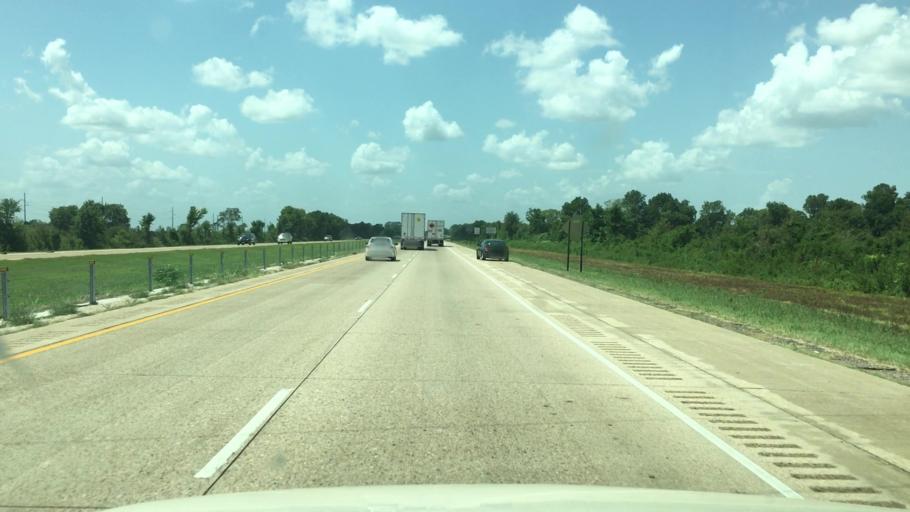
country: US
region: Arkansas
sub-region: Miller County
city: Texarkana
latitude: 33.5636
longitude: -93.8574
